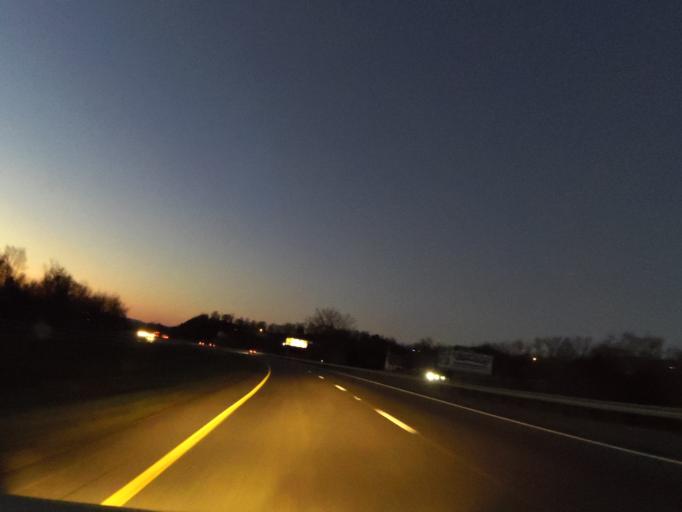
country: US
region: Tennessee
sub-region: Cocke County
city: Newport
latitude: 35.9804
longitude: -83.2740
